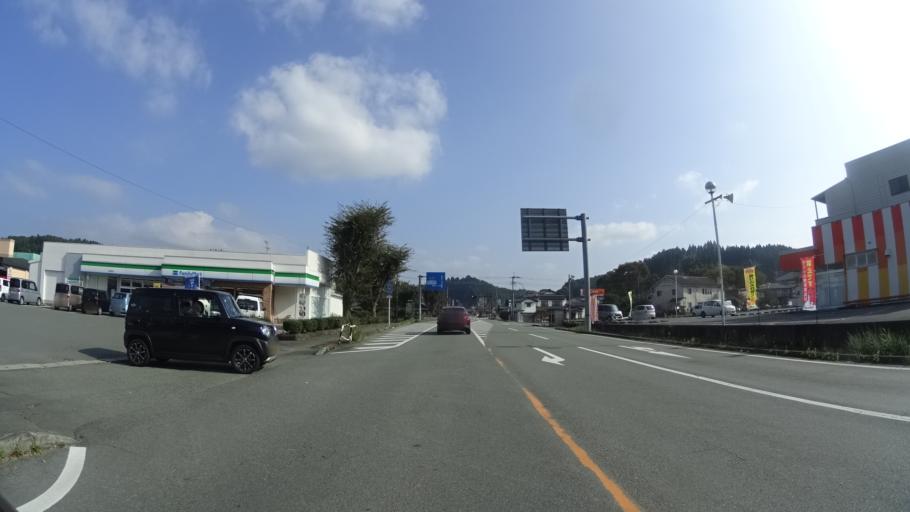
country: JP
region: Oita
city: Tsukawaki
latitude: 33.1236
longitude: 131.0631
